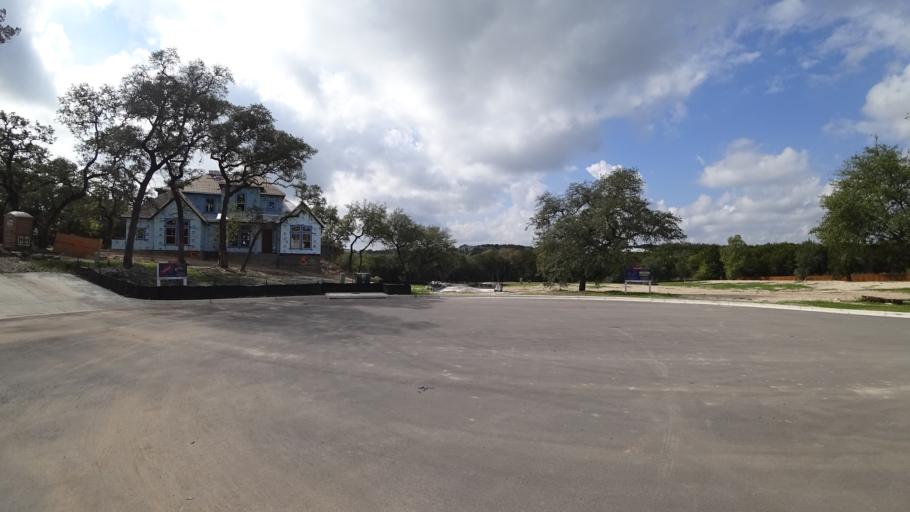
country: US
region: Texas
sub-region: Travis County
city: Barton Creek
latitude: 30.3108
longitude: -97.8814
